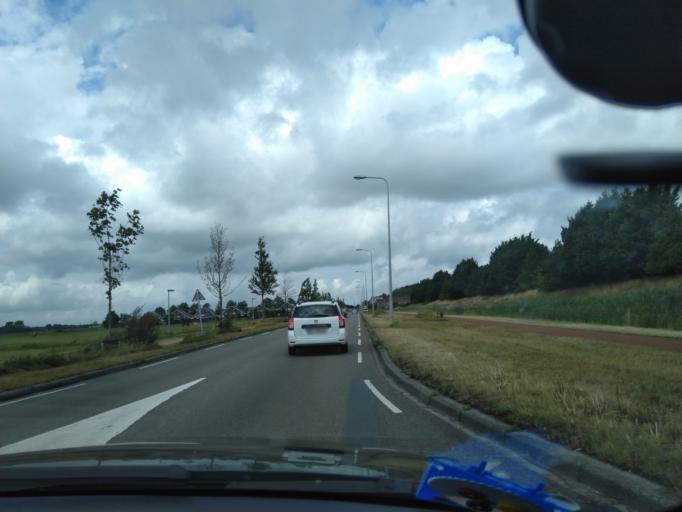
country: NL
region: Groningen
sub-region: Gemeente Groningen
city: Groningen
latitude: 53.2186
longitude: 6.5132
